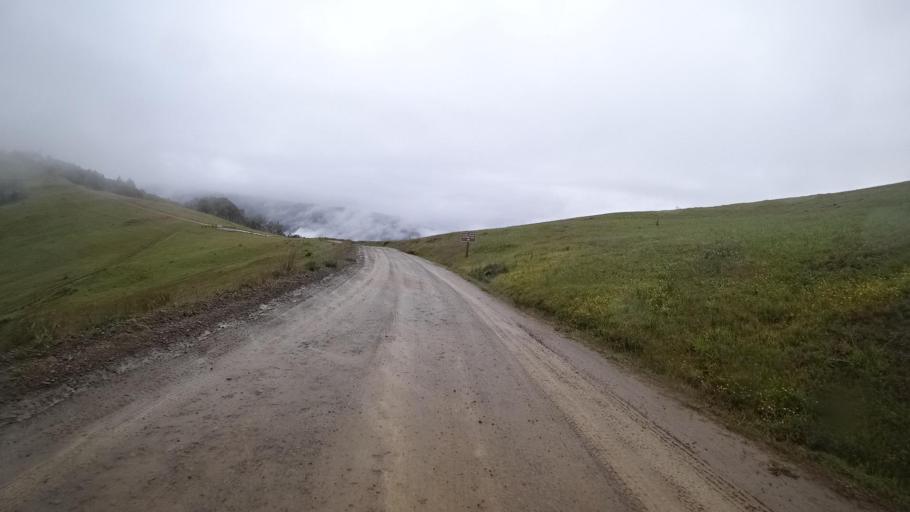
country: US
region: California
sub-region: Humboldt County
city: Westhaven-Moonstone
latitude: 41.1476
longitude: -123.8915
